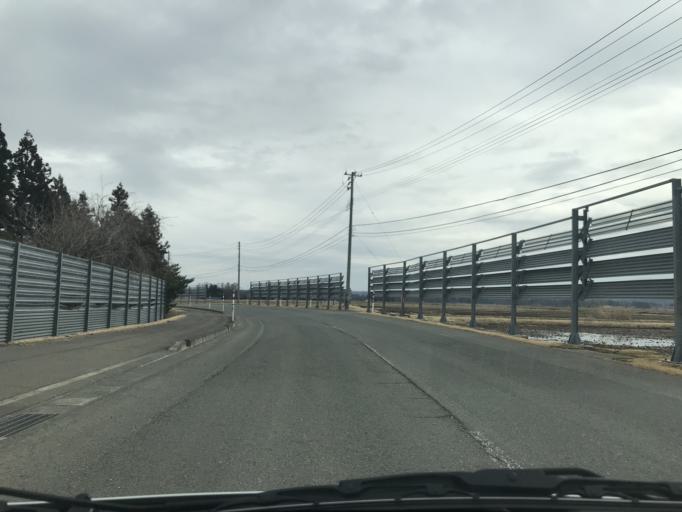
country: JP
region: Iwate
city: Kitakami
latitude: 39.3300
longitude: 140.9958
